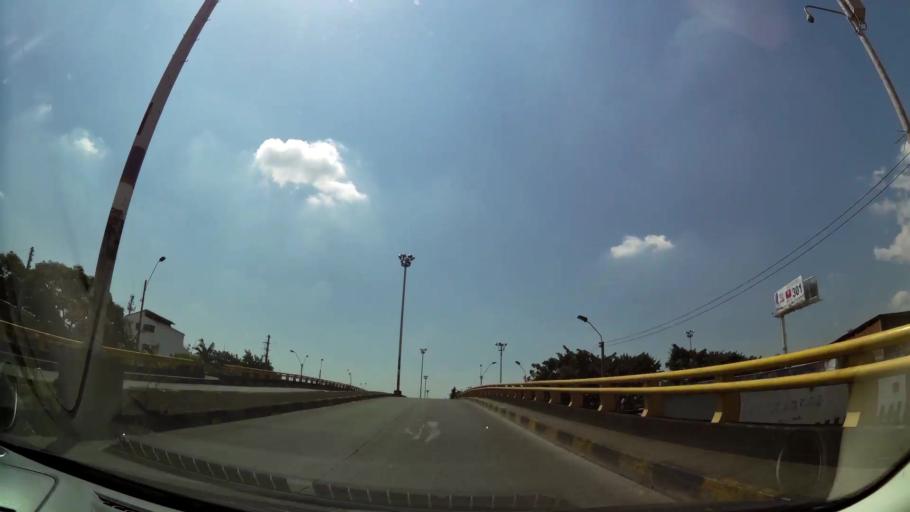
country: CO
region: Valle del Cauca
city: Cali
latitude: 3.4342
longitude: -76.5259
